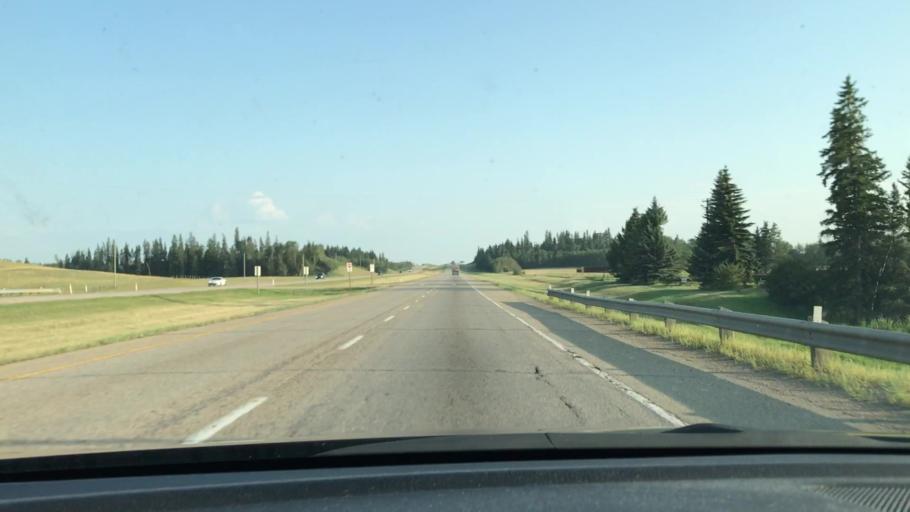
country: CA
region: Alberta
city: Ponoka
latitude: 52.6010
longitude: -113.6635
